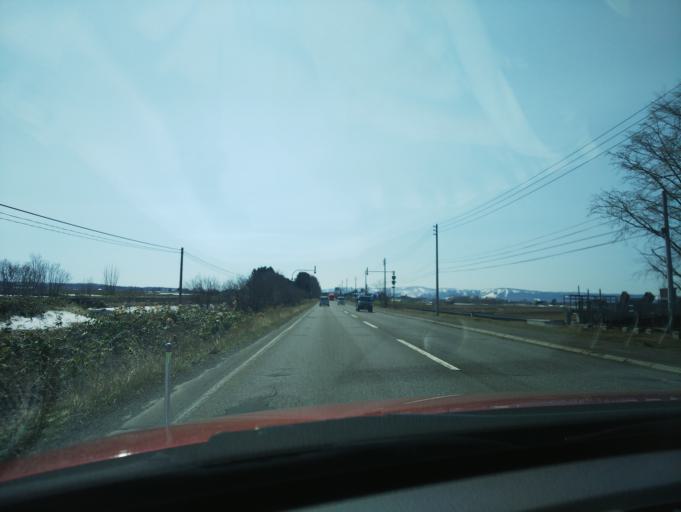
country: JP
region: Hokkaido
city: Nayoro
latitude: 44.3039
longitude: 142.4344
